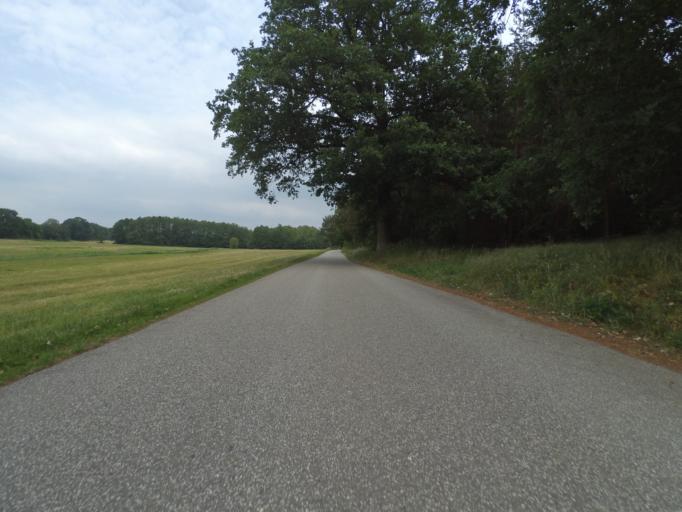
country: DE
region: Mecklenburg-Vorpommern
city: Lubz
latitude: 53.4138
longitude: 12.1355
